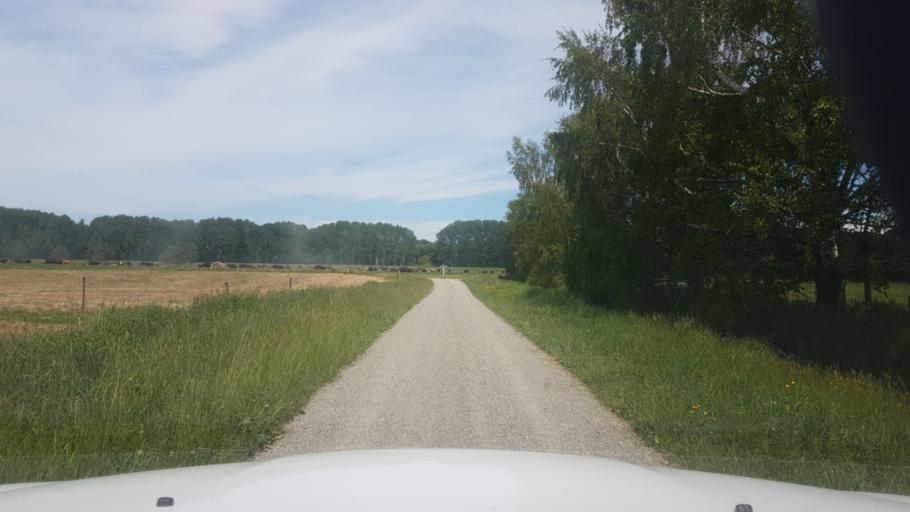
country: NZ
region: Canterbury
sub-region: Timaru District
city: Pleasant Point
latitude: -44.2228
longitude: 171.1201
